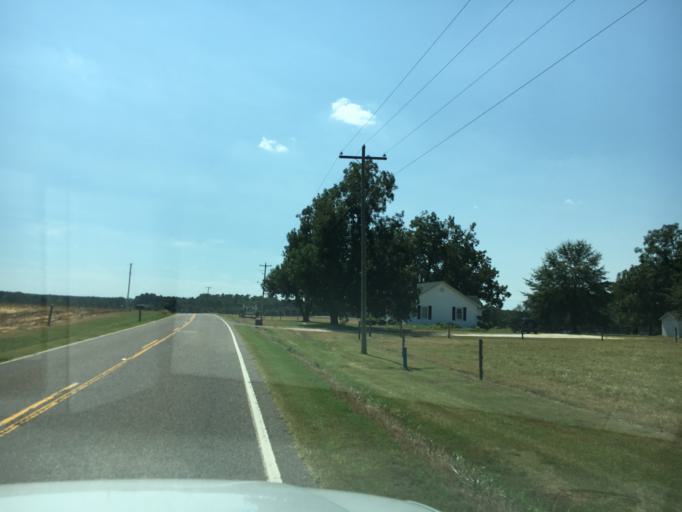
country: US
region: South Carolina
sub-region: Lexington County
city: Batesburg
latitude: 33.8358
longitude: -81.6620
